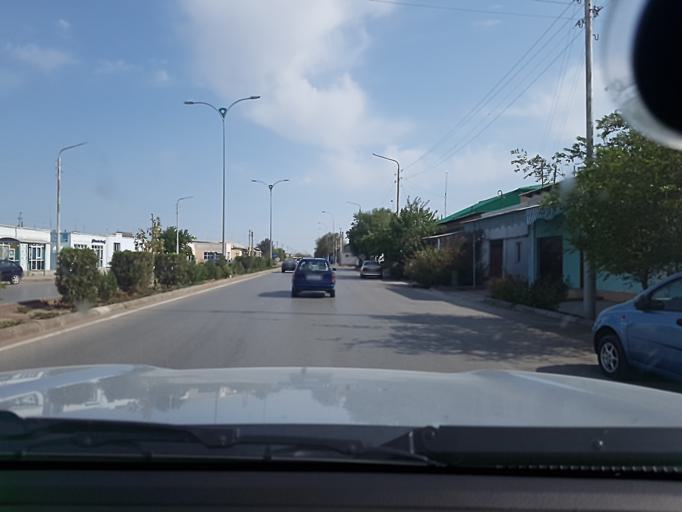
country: TM
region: Dasoguz
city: Dasoguz
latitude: 41.8322
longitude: 59.9831
